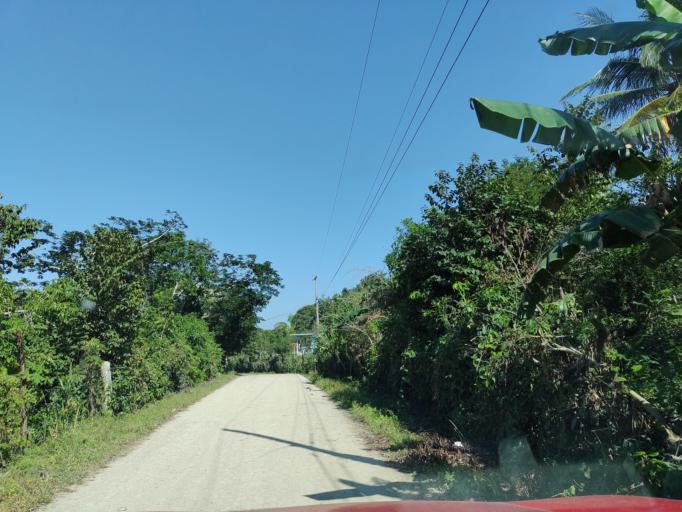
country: MX
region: Veracruz
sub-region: Papantla
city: Polutla
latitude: 20.4906
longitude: -97.1847
